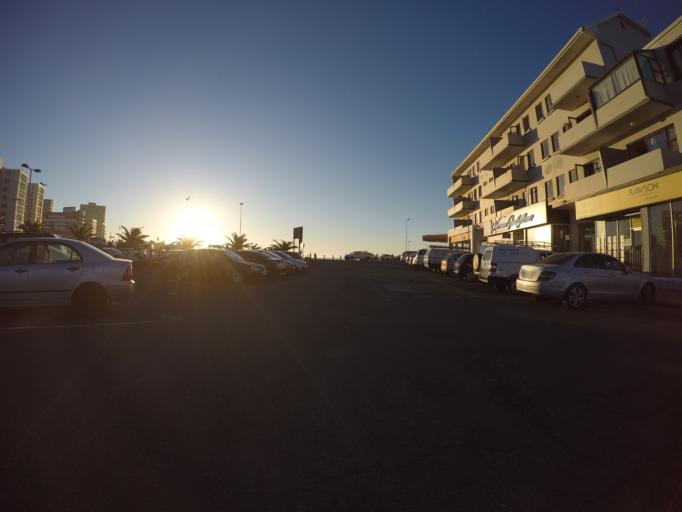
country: ZA
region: Western Cape
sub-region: City of Cape Town
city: Cape Town
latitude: -33.9059
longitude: 18.3990
